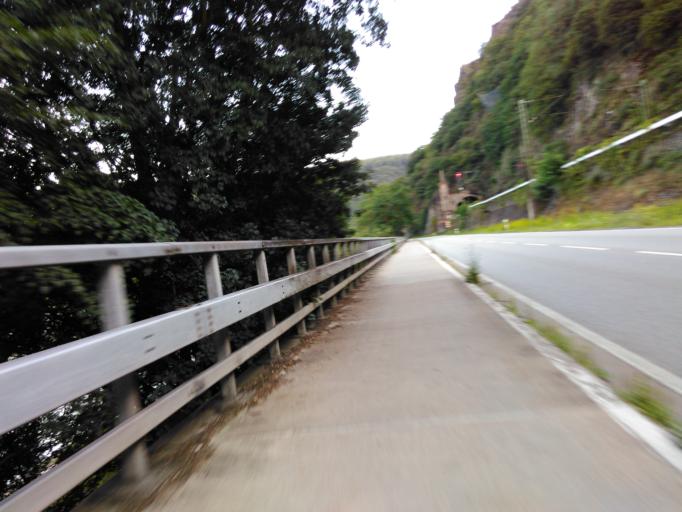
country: DE
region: Rheinland-Pfalz
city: Sankt Goarshausen
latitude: 50.1330
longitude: 7.7359
